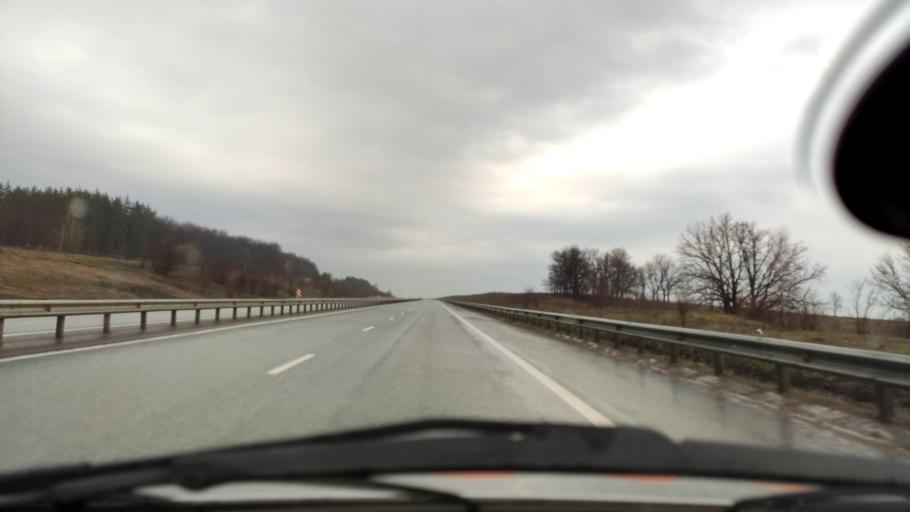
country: RU
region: Bashkortostan
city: Tolbazy
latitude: 53.8570
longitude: 55.9201
